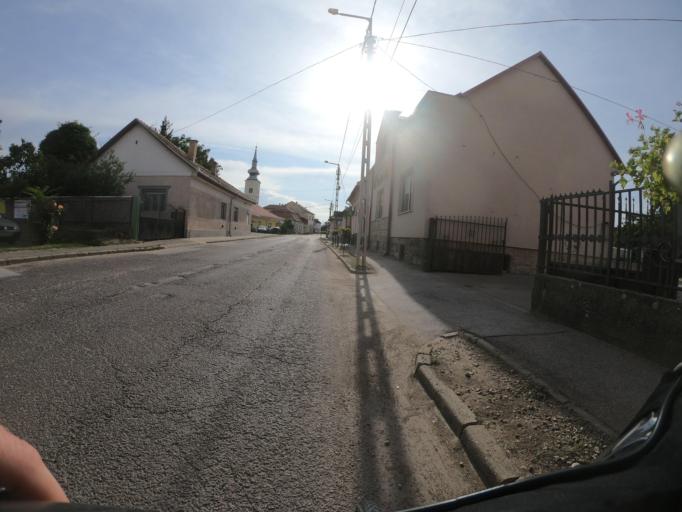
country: HU
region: Borsod-Abauj-Zemplen
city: Mezocsat
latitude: 47.8212
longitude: 20.9058
